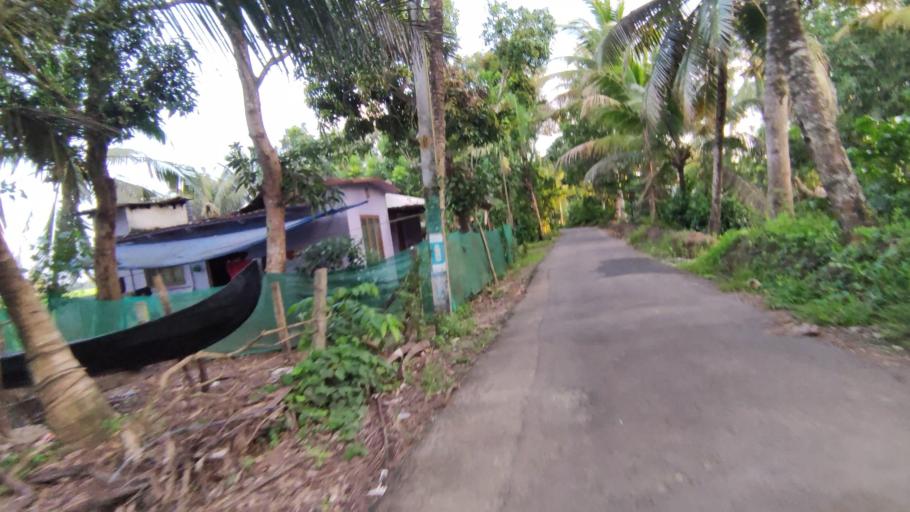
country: IN
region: Kerala
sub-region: Kottayam
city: Kottayam
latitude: 9.5830
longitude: 76.4482
